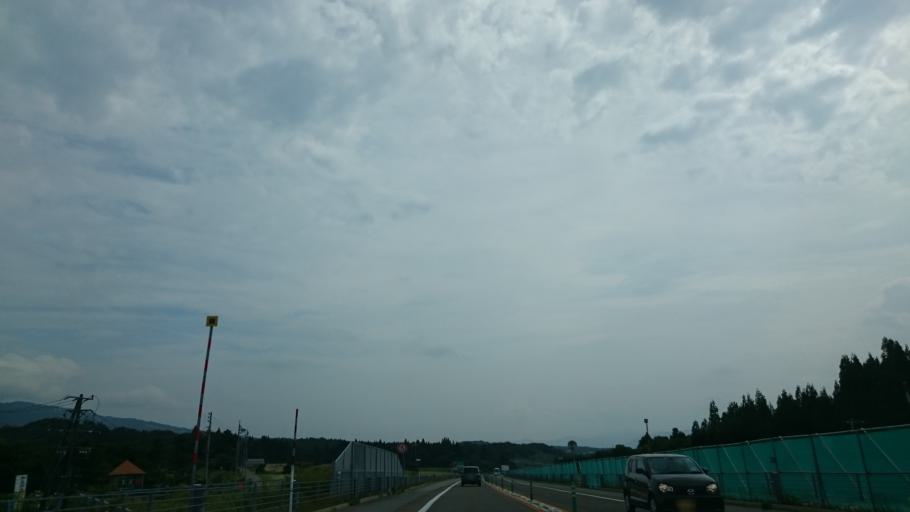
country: JP
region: Gifu
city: Gujo
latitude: 36.0033
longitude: 136.9277
